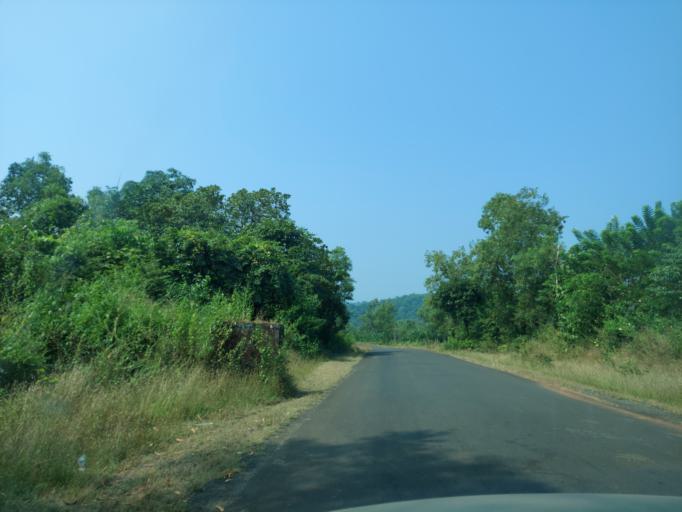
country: IN
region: Maharashtra
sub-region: Sindhudurg
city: Kudal
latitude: 15.9772
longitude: 73.6156
